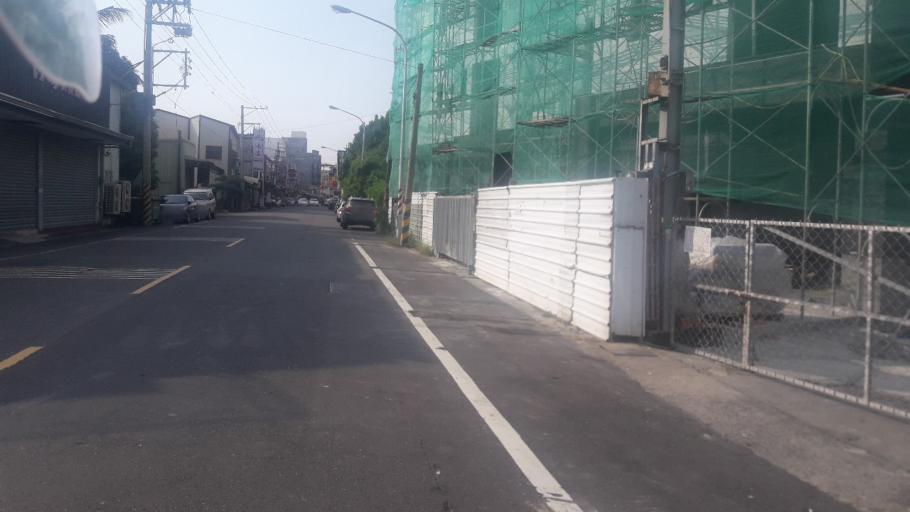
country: TW
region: Taiwan
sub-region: Tainan
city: Tainan
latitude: 22.8560
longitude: 120.2641
